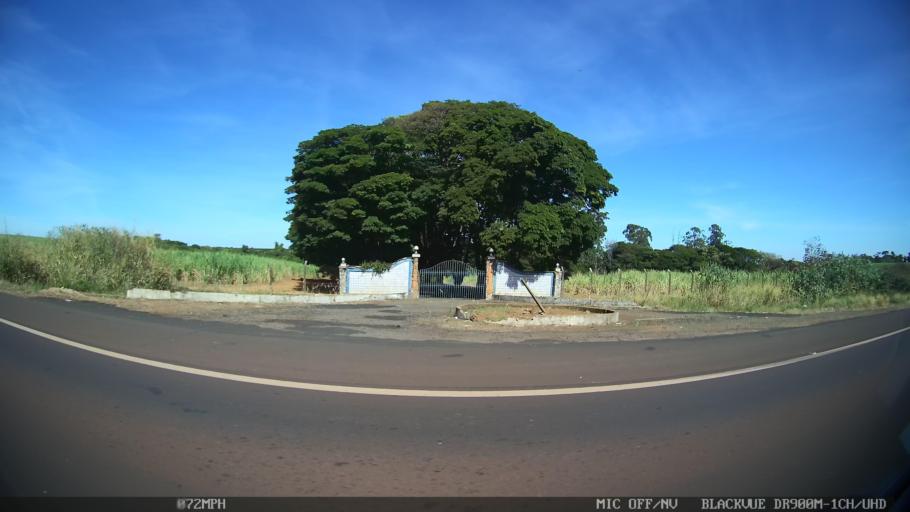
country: BR
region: Sao Paulo
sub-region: Franca
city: Franca
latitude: -20.5562
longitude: -47.5670
